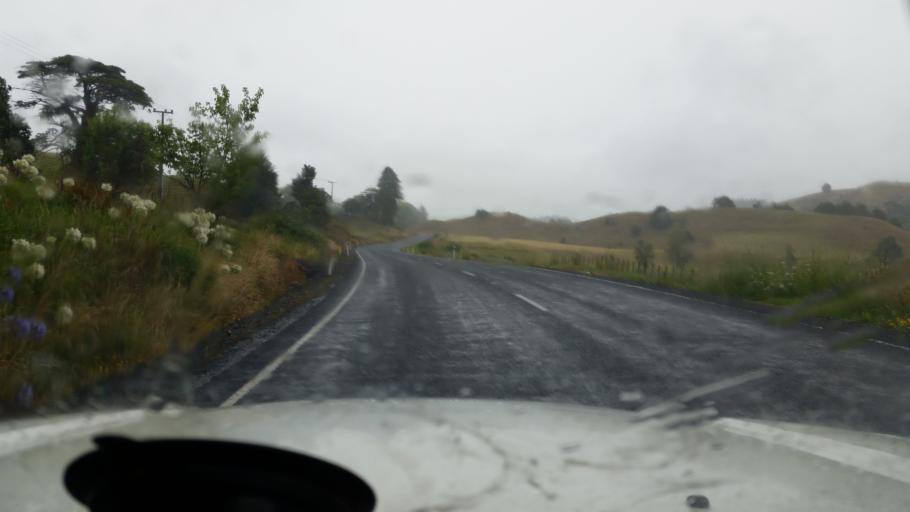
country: NZ
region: Northland
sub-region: Far North District
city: Kaitaia
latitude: -35.2733
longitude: 173.3539
